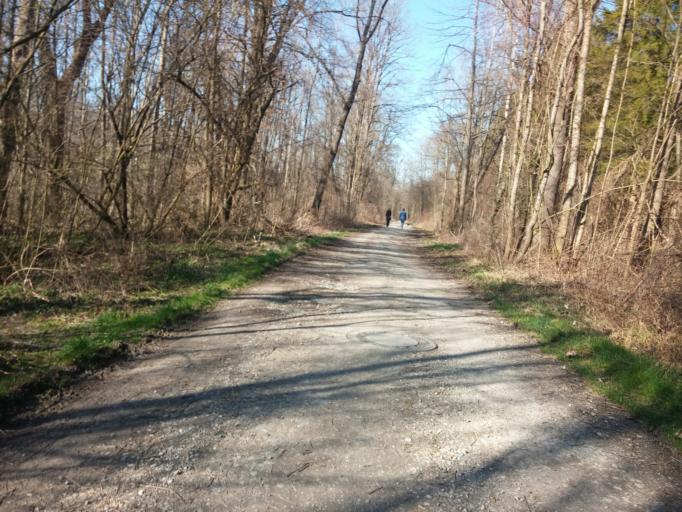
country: DE
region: Bavaria
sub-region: Upper Bavaria
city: Ismaning
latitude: 48.2412
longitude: 11.6745
